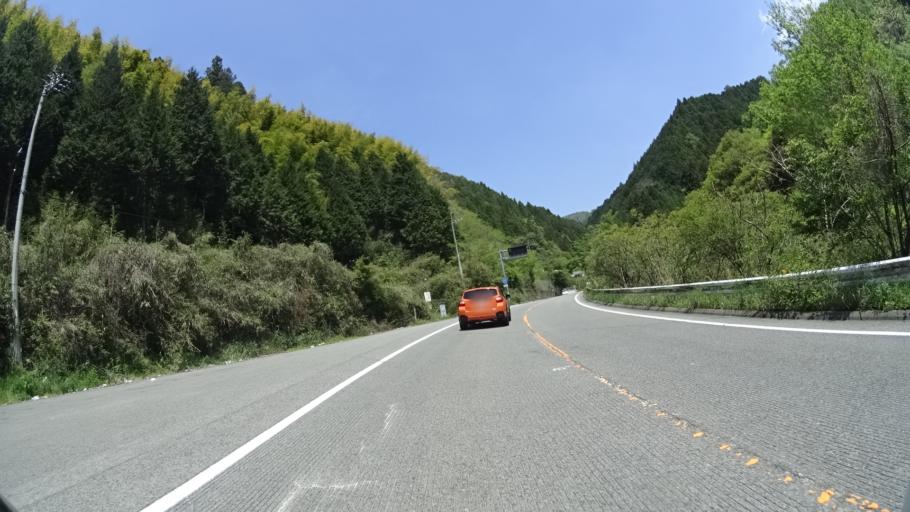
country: JP
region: Ehime
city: Hojo
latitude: 33.9306
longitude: 132.8962
